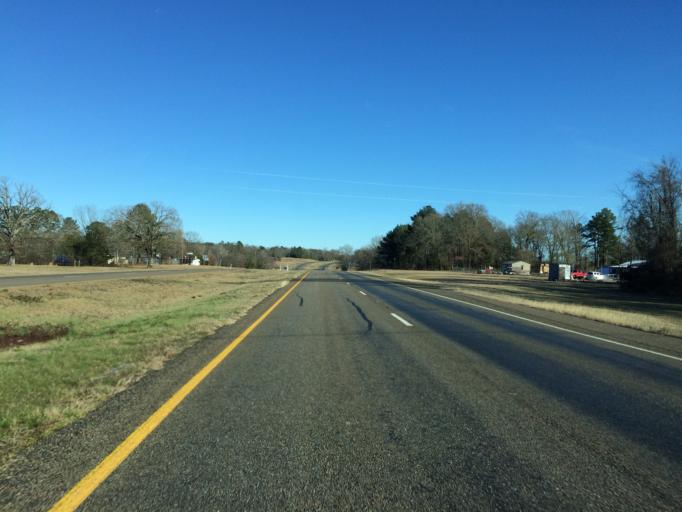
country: US
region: Texas
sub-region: Wood County
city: Hawkins
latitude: 32.5947
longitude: -95.2396
